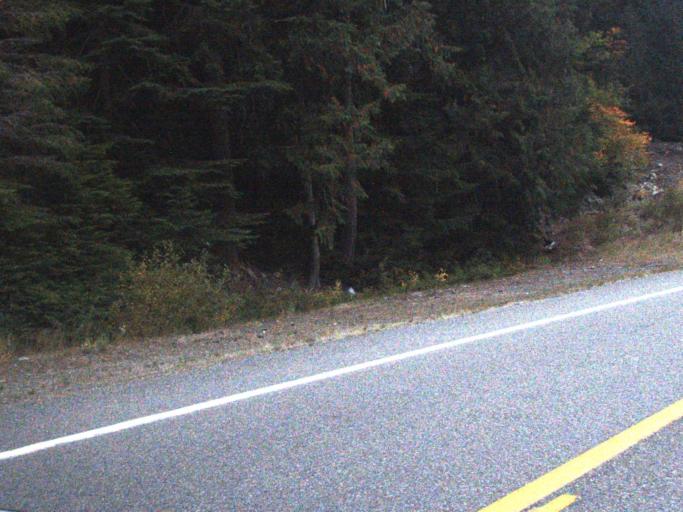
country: US
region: Washington
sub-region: Snohomish County
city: Darrington
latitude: 48.6807
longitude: -120.8824
